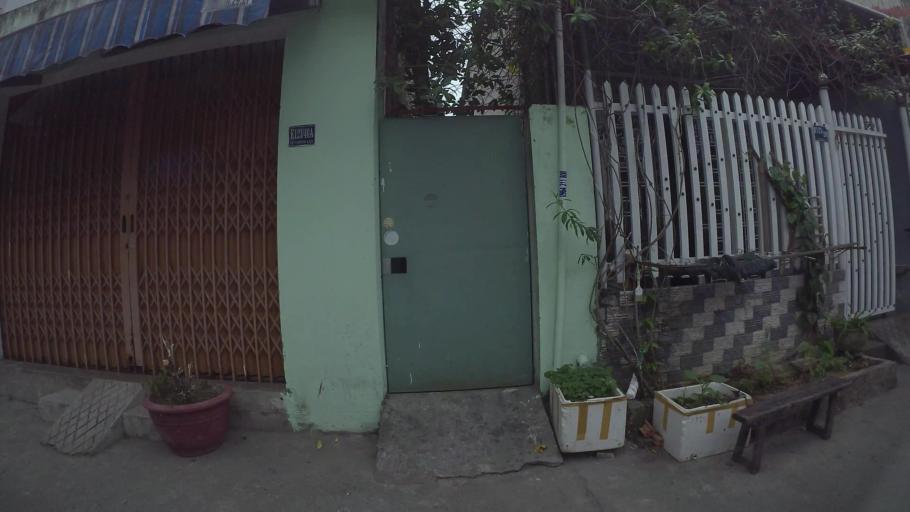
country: VN
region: Da Nang
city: Thanh Khe
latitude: 16.0631
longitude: 108.1867
